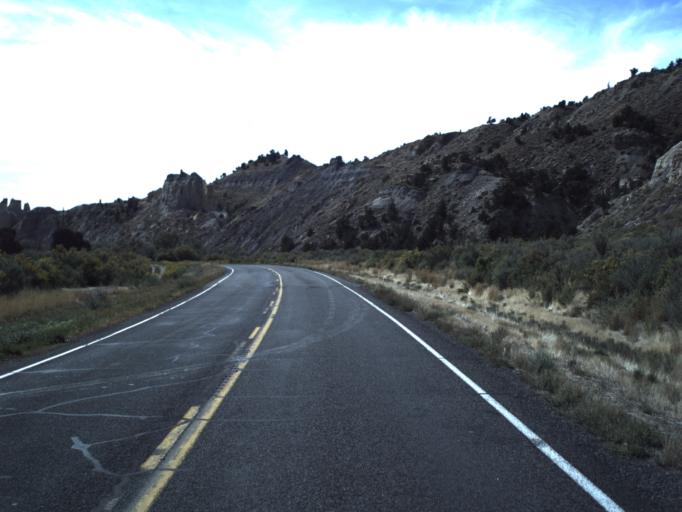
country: US
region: Utah
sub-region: Garfield County
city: Panguitch
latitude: 37.5930
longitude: -112.0623
